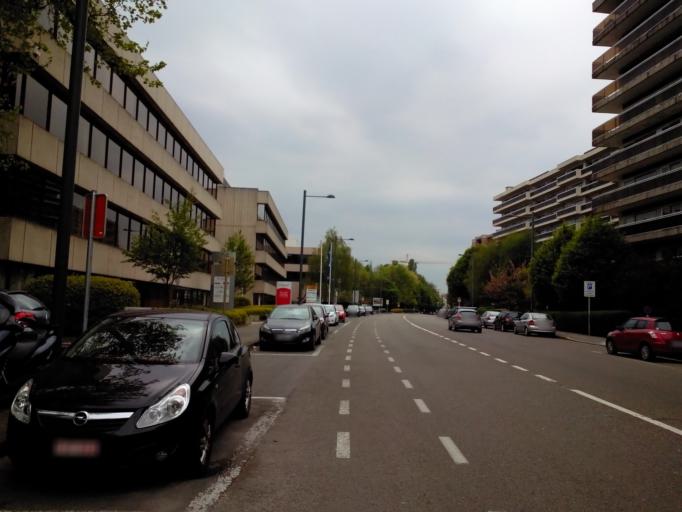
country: BE
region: Flanders
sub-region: Provincie Vlaams-Brabant
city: Diegem
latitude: 50.8529
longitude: 4.4110
